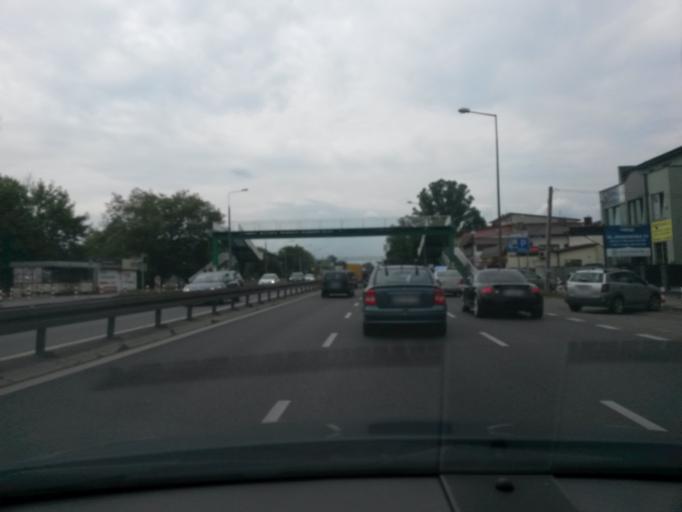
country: PL
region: Masovian Voivodeship
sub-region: Powiat pruszkowski
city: Raszyn
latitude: 52.1560
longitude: 20.9223
